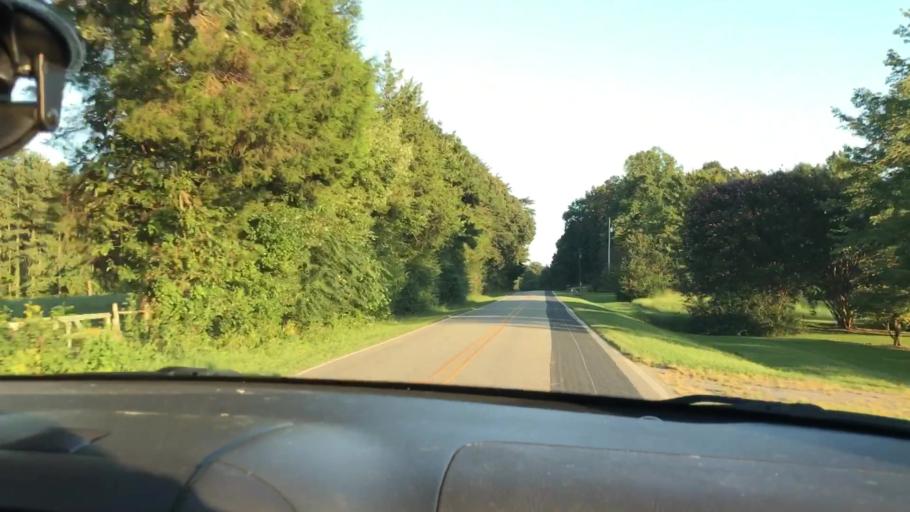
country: US
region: North Carolina
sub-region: Randolph County
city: Ramseur
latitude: 35.7845
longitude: -79.6411
